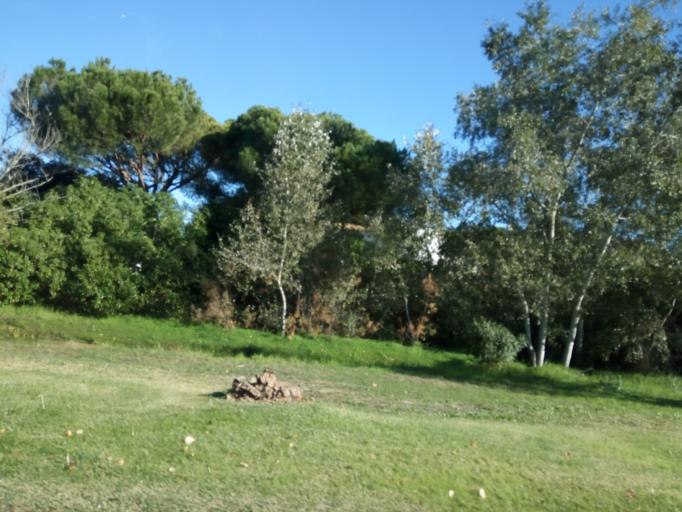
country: PT
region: Faro
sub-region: Loule
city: Vilamoura
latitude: 37.0855
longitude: -8.1191
